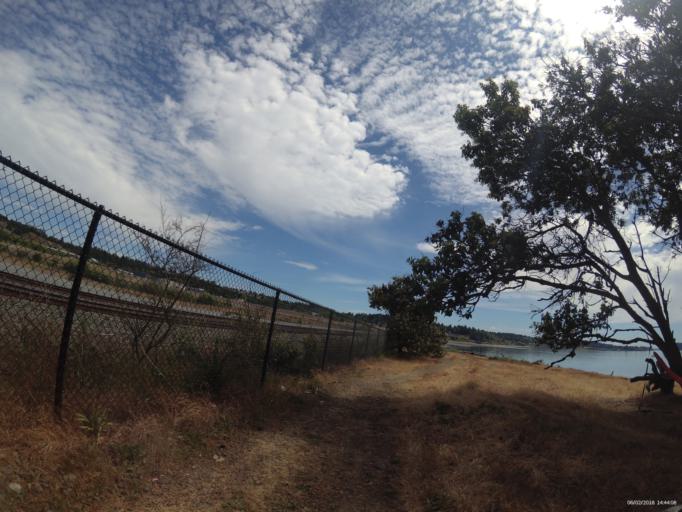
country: US
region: Washington
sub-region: Pierce County
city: Steilacoom
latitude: 47.1979
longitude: -122.5826
